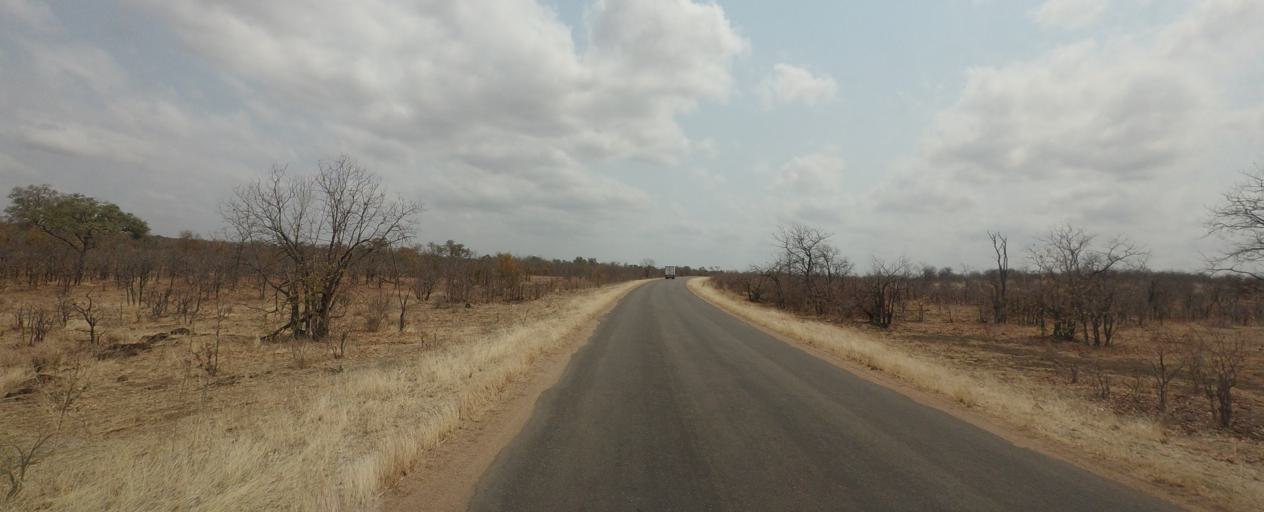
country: ZA
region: Limpopo
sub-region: Mopani District Municipality
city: Phalaborwa
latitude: -23.6082
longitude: 31.4551
